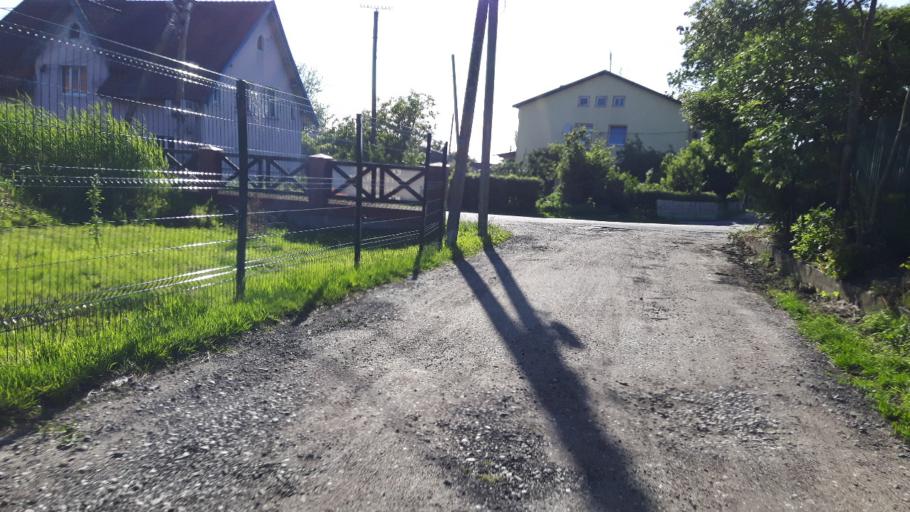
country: LT
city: Nida
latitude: 55.1533
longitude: 20.8560
